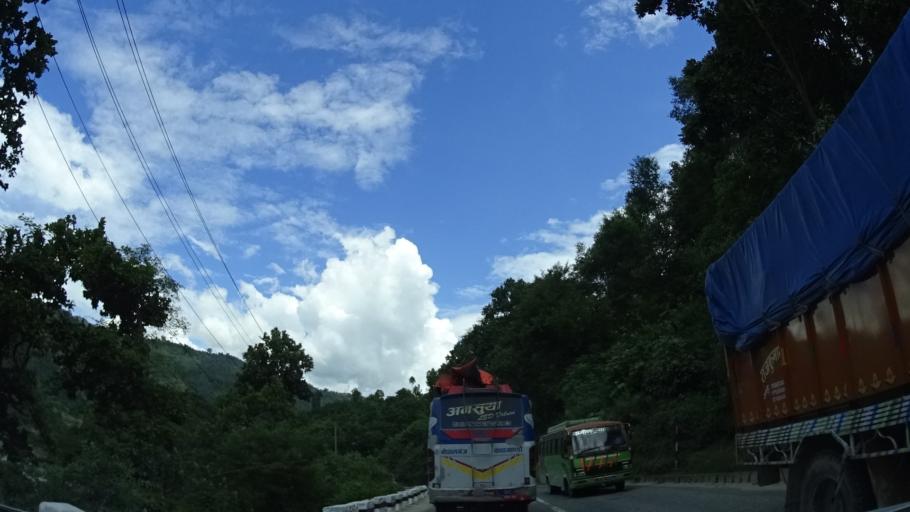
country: NP
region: Central Region
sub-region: Narayani Zone
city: Hitura
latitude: 27.8033
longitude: 84.8471
